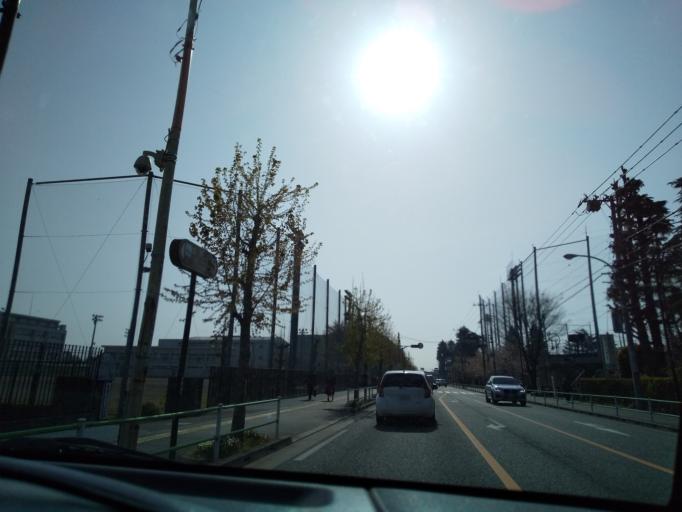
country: JP
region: Tokyo
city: Hino
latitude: 35.7043
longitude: 139.3848
